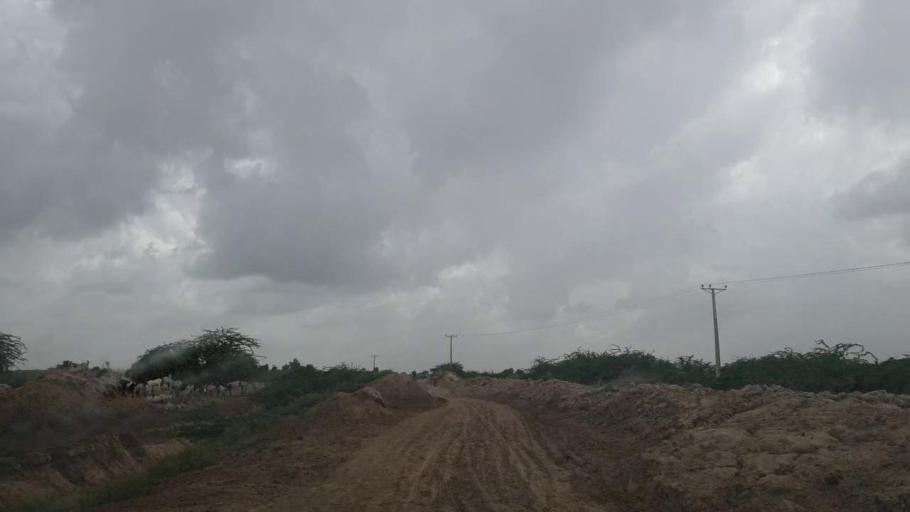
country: PK
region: Sindh
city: Naukot
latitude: 24.8563
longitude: 69.2064
